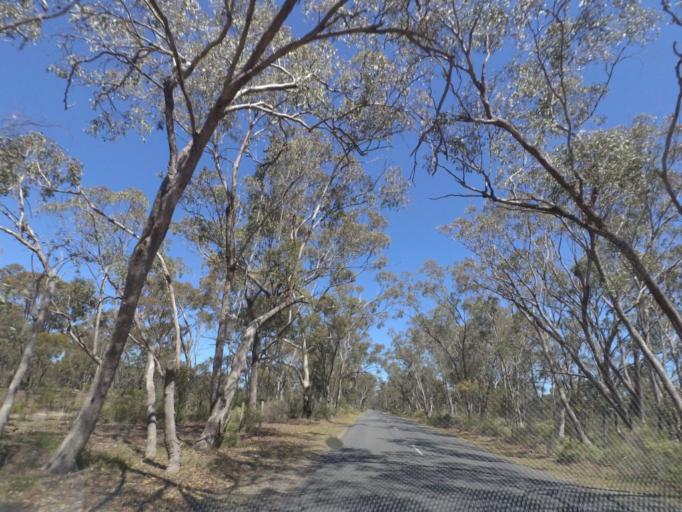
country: AU
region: Victoria
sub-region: Melton
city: Melton West
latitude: -37.6516
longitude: 144.5076
